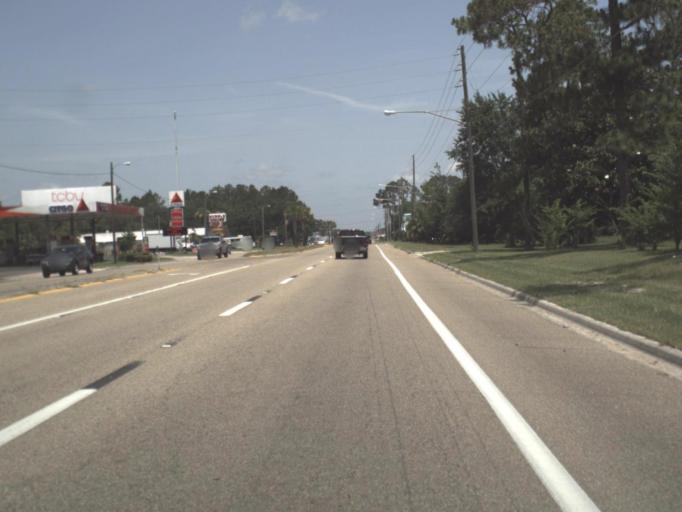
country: US
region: Florida
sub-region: Taylor County
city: Perry
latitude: 30.0862
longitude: -83.5707
